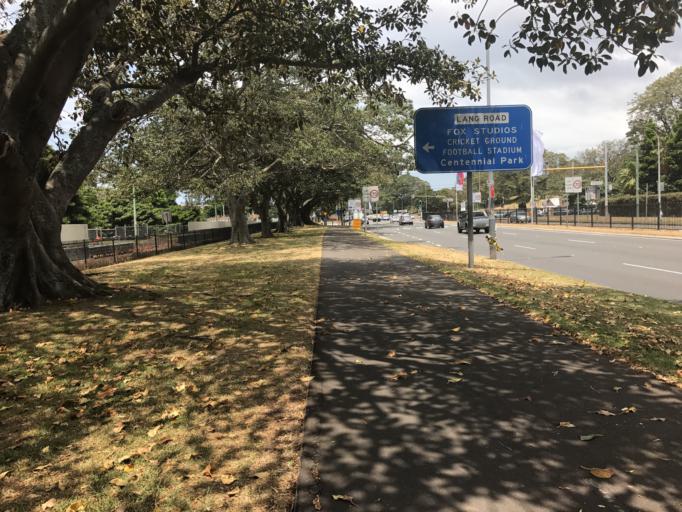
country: AU
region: New South Wales
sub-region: Woollahra
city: Paddington
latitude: -33.8940
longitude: 151.2215
